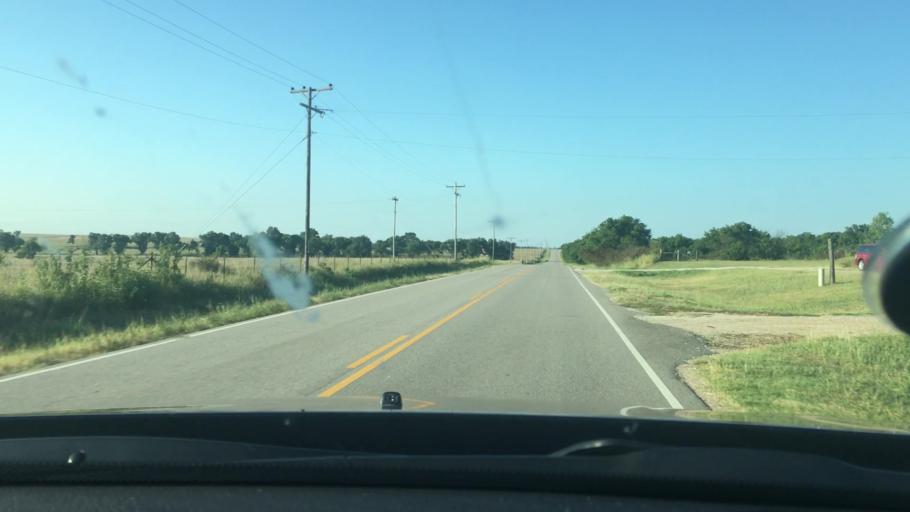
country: US
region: Oklahoma
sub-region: Murray County
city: Sulphur
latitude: 34.6043
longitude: -96.8449
